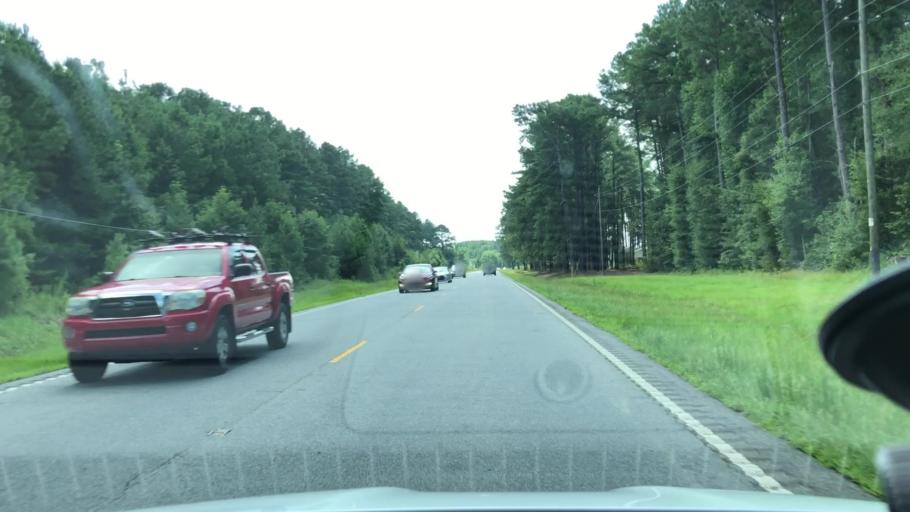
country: US
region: North Carolina
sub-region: Beaufort County
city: Washington
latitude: 35.6693
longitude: -77.0759
